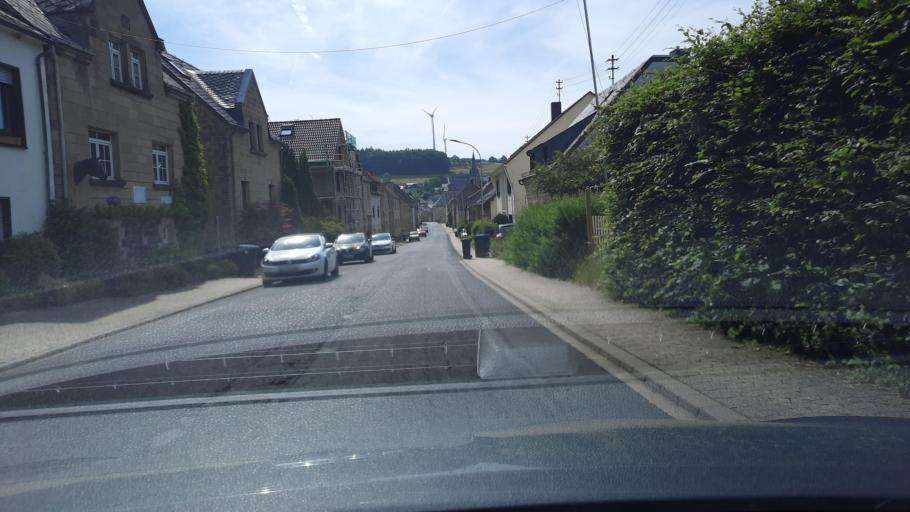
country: DE
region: Rheinland-Pfalz
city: Kempenich
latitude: 50.4084
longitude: 7.1392
